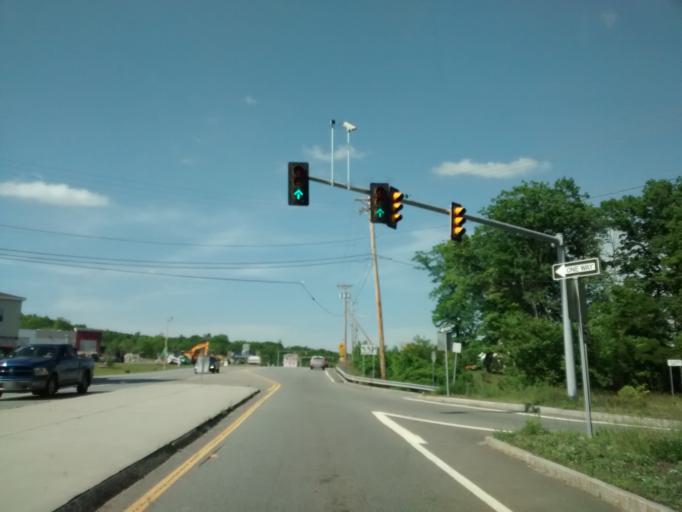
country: US
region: Massachusetts
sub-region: Worcester County
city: Shrewsbury
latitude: 42.2839
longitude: -71.6694
